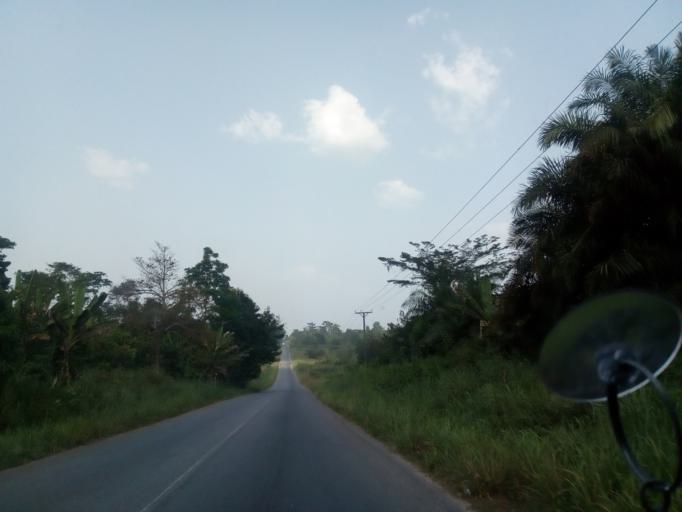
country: GH
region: Eastern
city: Suhum
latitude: 6.0508
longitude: -0.4082
